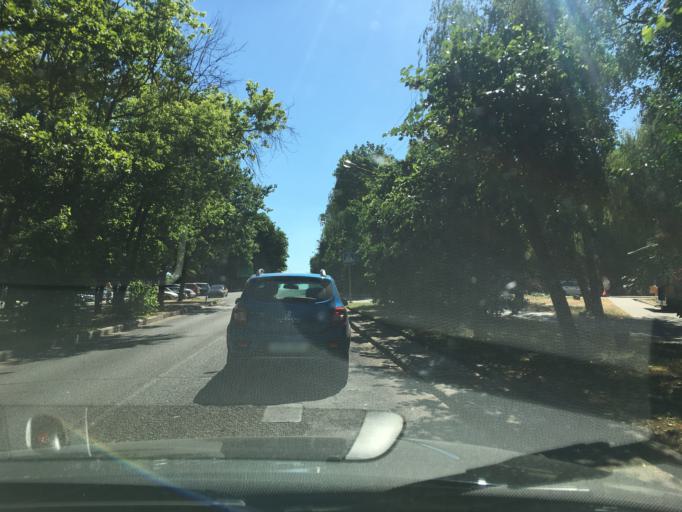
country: BY
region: Grodnenskaya
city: Hrodna
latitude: 53.6950
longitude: 23.8456
